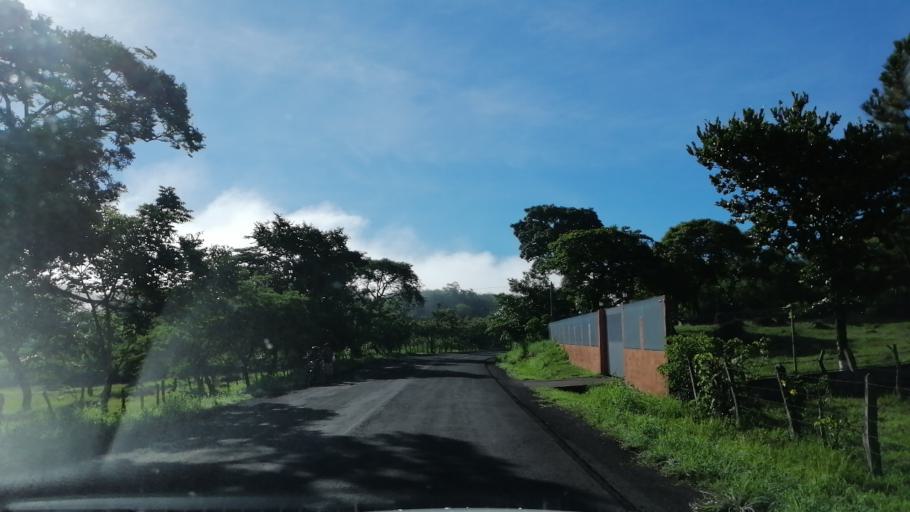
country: SV
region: Morazan
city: Cacaopera
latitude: 13.7782
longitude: -88.0989
